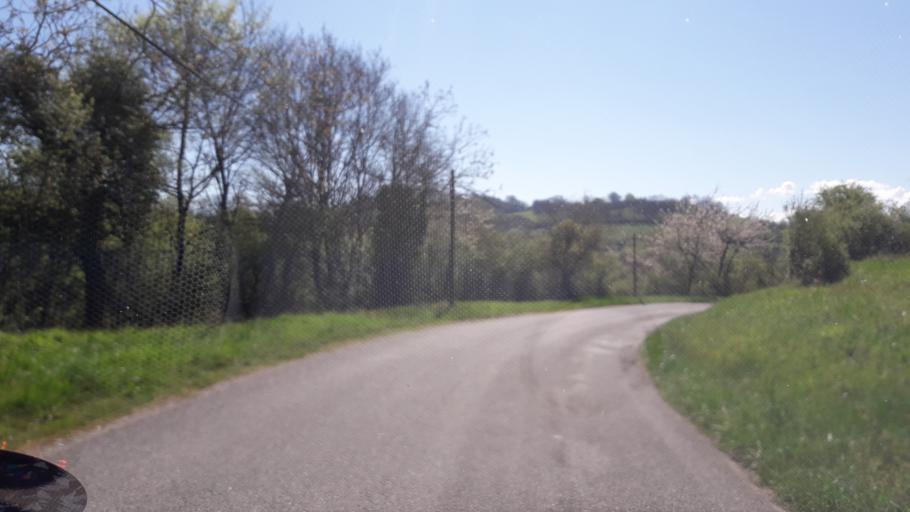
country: FR
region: Midi-Pyrenees
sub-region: Departement de la Haute-Garonne
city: Montesquieu-Volvestre
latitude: 43.1628
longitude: 1.3185
